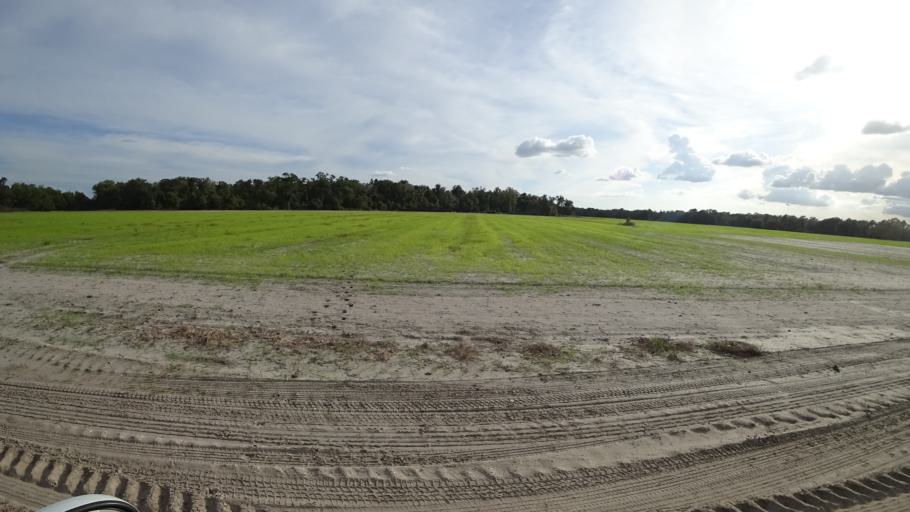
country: US
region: Florida
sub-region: Hillsborough County
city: Wimauma
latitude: 27.5664
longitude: -82.0873
